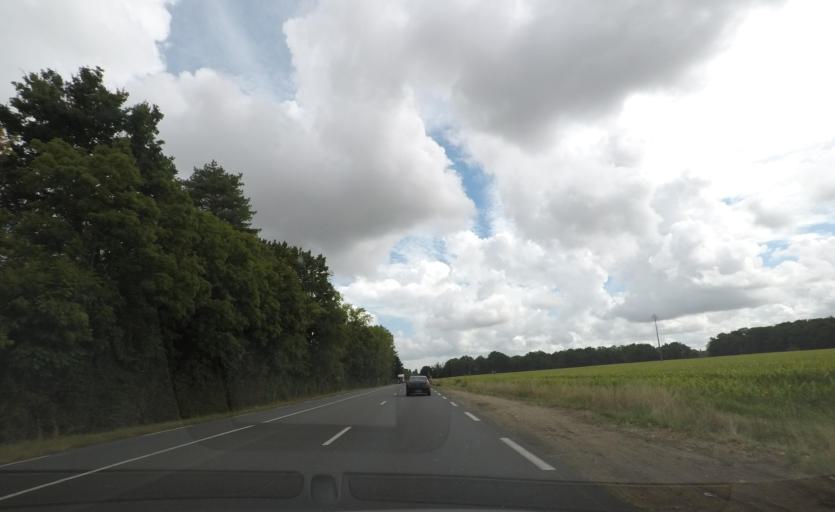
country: FR
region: Pays de la Loire
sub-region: Departement de Maine-et-Loire
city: Pellouailles-les-Vignes
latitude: 47.5288
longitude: -0.4227
